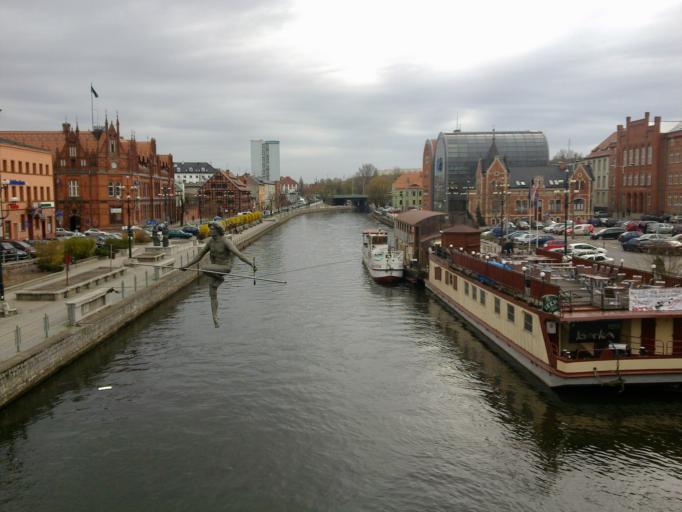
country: PL
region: Kujawsko-Pomorskie
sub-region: Bydgoszcz
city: Bydgoszcz
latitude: 53.1233
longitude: 18.0016
